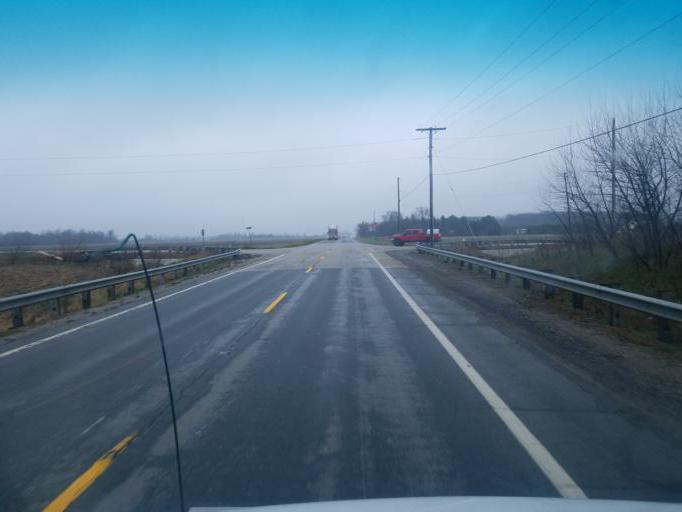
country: US
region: Ohio
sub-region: Wood County
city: Weston
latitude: 41.3723
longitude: -83.7677
